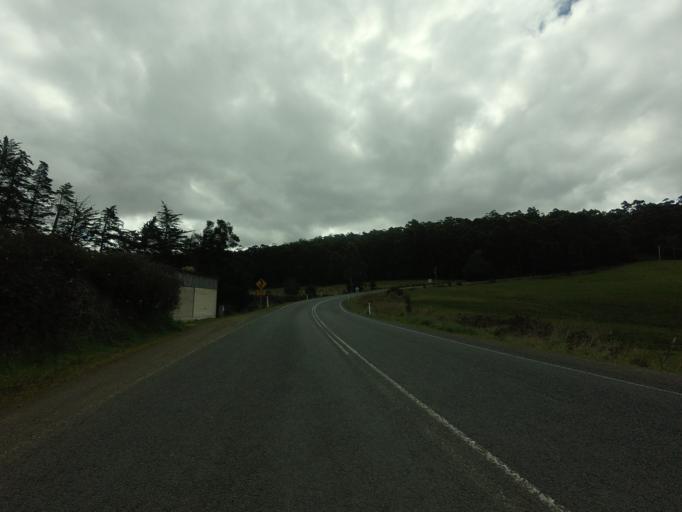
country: AU
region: Tasmania
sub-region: Huon Valley
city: Geeveston
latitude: -43.4123
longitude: 146.9543
